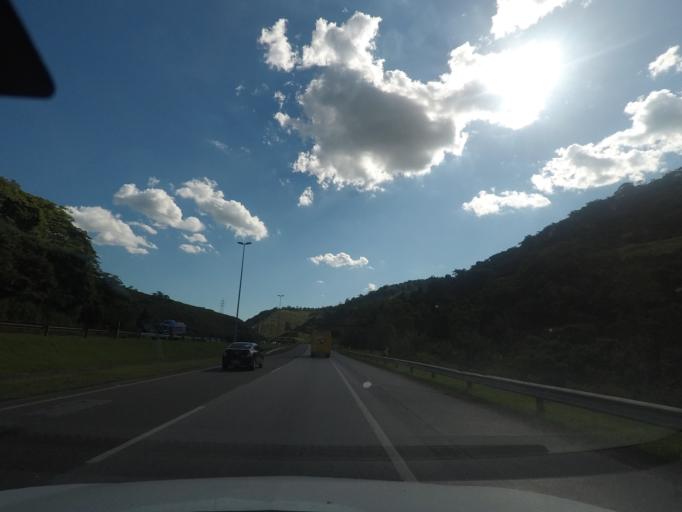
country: BR
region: Rio de Janeiro
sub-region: Guapimirim
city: Guapimirim
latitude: -22.5707
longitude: -43.0061
